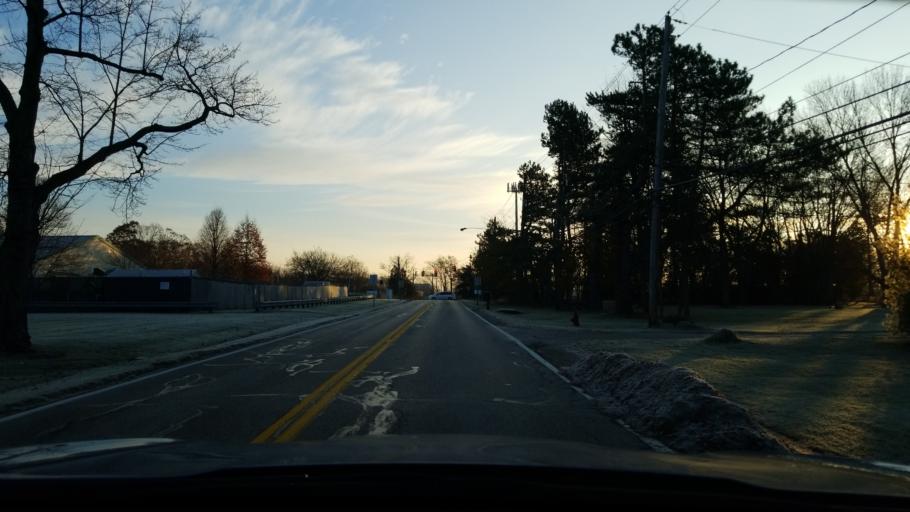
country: US
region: Ohio
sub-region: Cuyahoga County
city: Fairview Park
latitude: 41.4066
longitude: -81.8738
